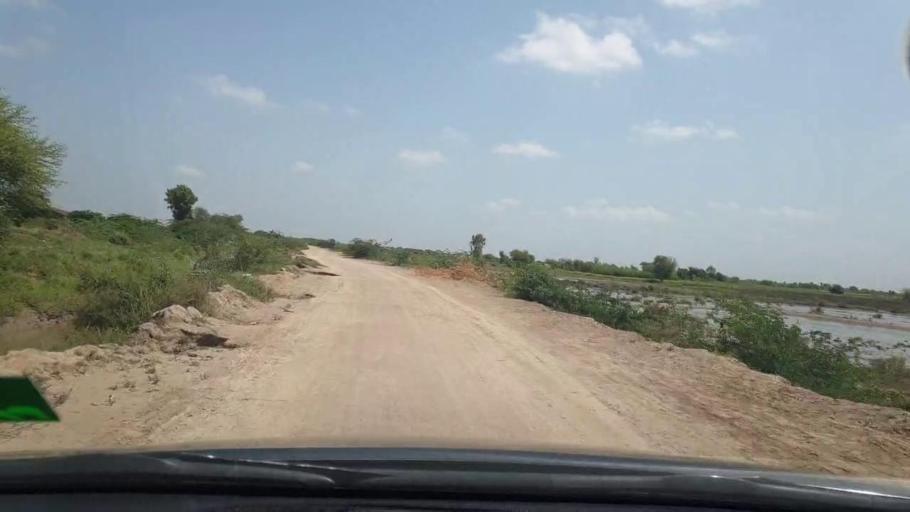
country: PK
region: Sindh
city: Tando Bago
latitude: 24.8780
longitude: 69.0902
